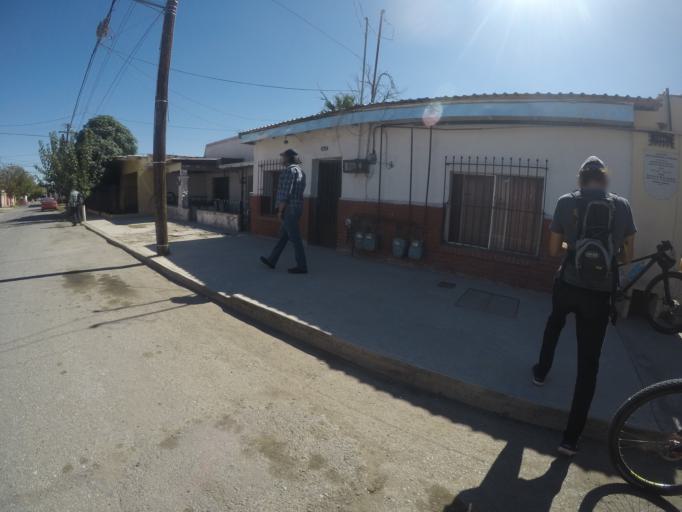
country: MX
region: Chihuahua
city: Ciudad Juarez
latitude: 31.7397
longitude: -106.4716
